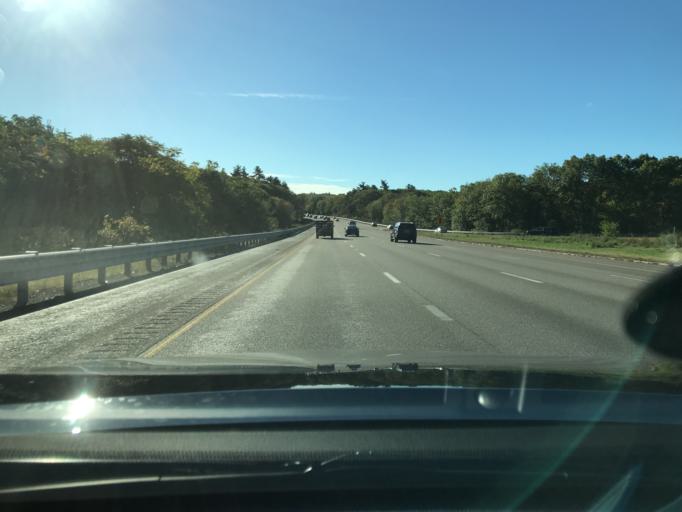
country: US
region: Massachusetts
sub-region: Norfolk County
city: Westwood
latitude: 42.2422
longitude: -71.2042
